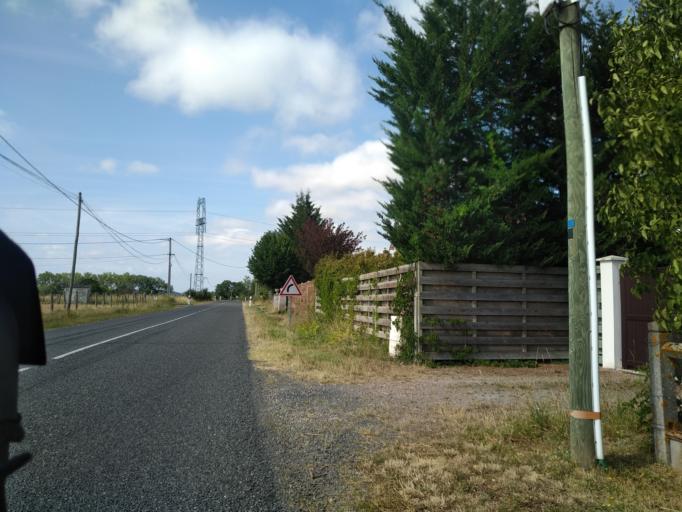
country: FR
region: Auvergne
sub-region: Departement de l'Allier
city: Saint-Pourcain-sur-Sioule
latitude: 46.2802
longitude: 3.2336
